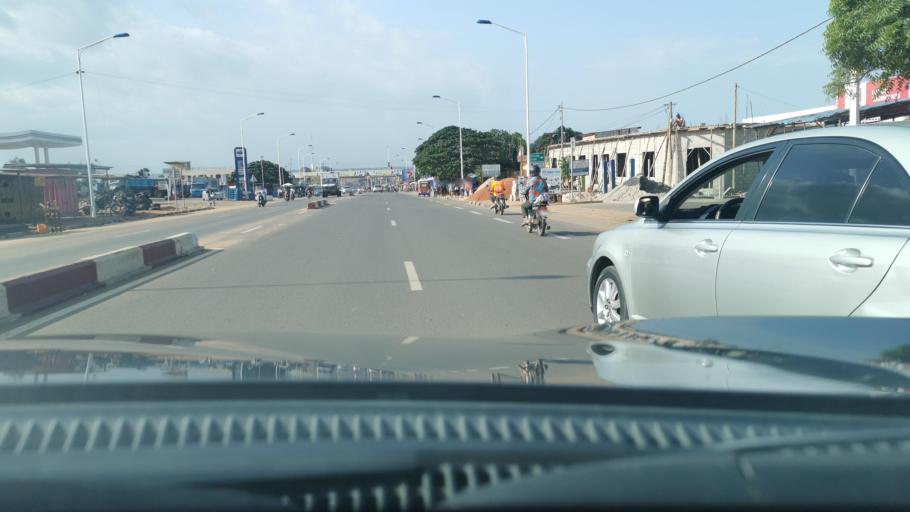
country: TG
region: Maritime
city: Lome
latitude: 6.2088
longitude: 1.2436
